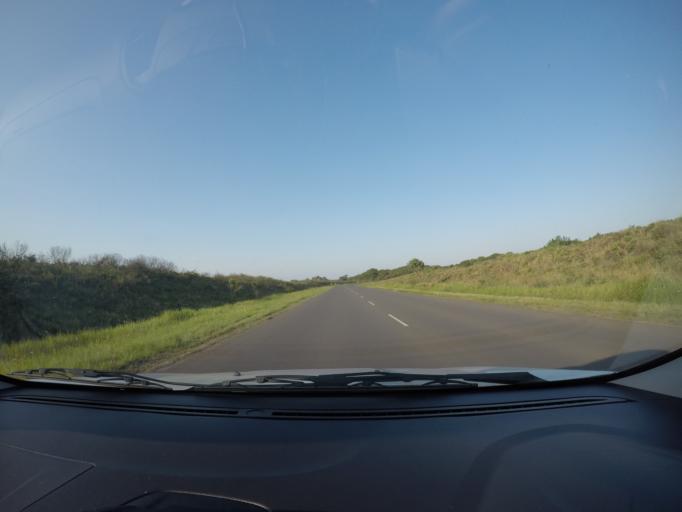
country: ZA
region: KwaZulu-Natal
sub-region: uThungulu District Municipality
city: Richards Bay
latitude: -28.7492
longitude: 32.0115
